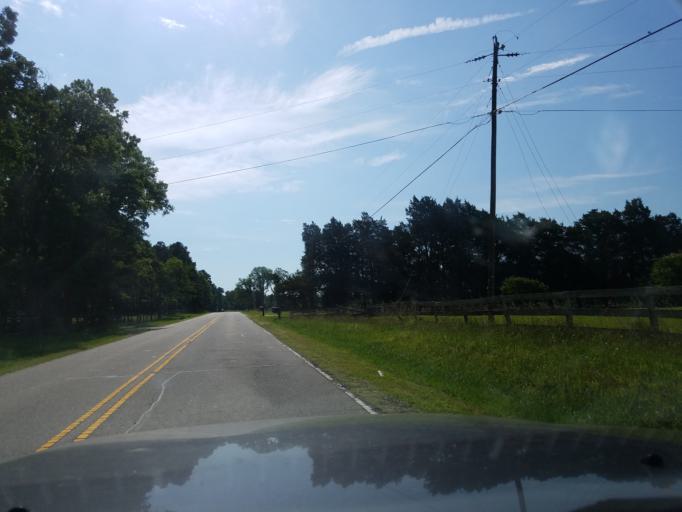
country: US
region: North Carolina
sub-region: Granville County
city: Oxford
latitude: 36.3148
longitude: -78.5281
